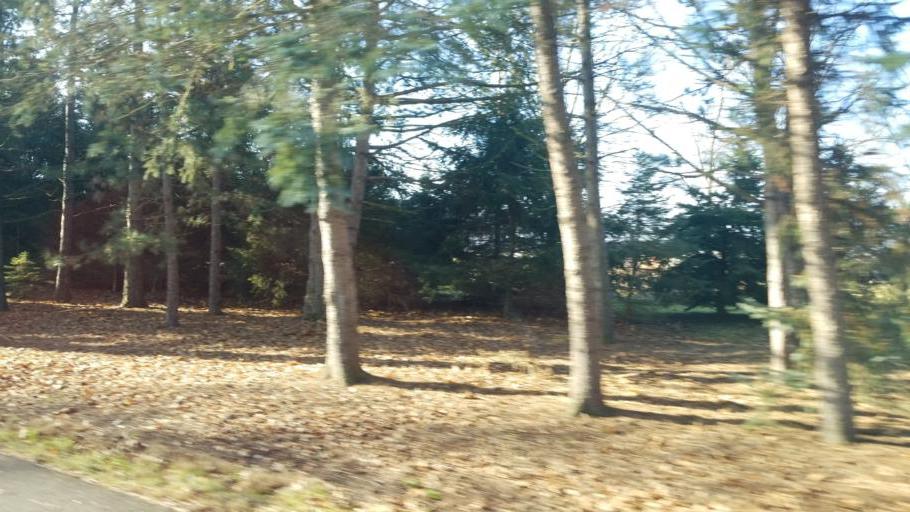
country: US
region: Ohio
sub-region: Seneca County
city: Tiffin
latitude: 41.0773
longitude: -83.1127
